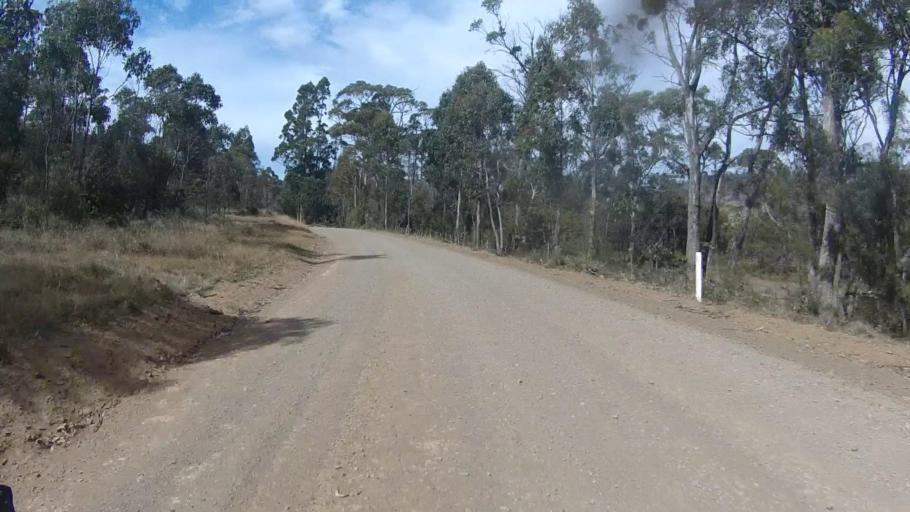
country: AU
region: Tasmania
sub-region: Sorell
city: Sorell
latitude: -42.6498
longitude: 147.8983
